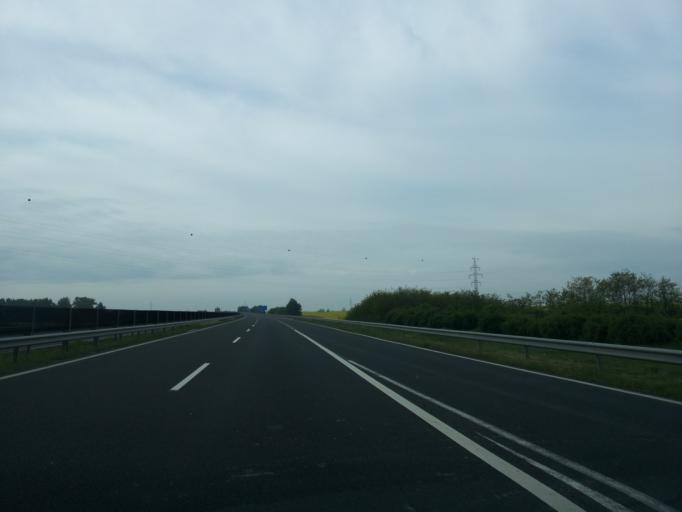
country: HU
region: Fejer
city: dunaujvaros
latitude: 46.9908
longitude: 18.8848
